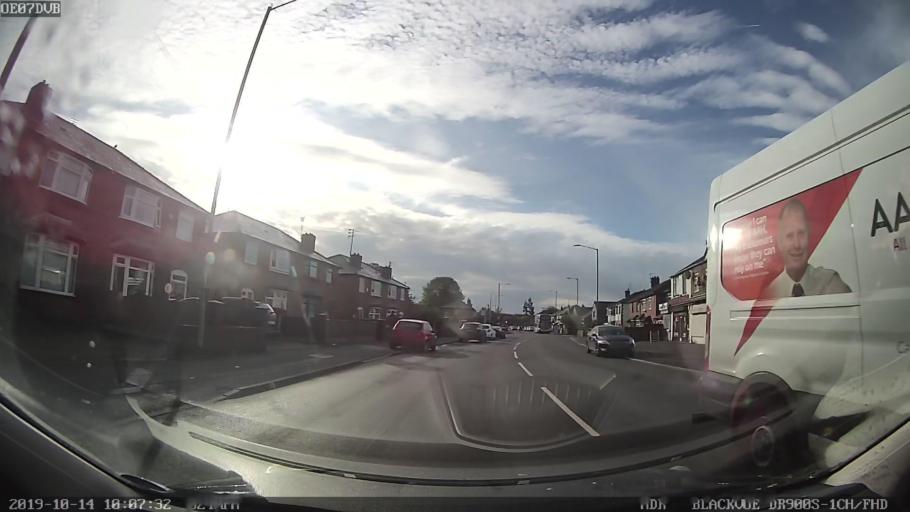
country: GB
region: England
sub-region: Manchester
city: Failsworth
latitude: 53.5222
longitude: -2.1819
